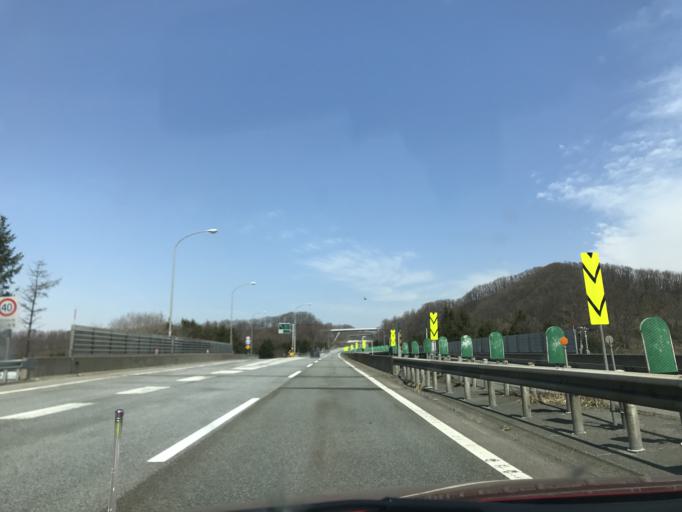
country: JP
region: Hokkaido
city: Iwamizawa
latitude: 43.2414
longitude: 141.8303
